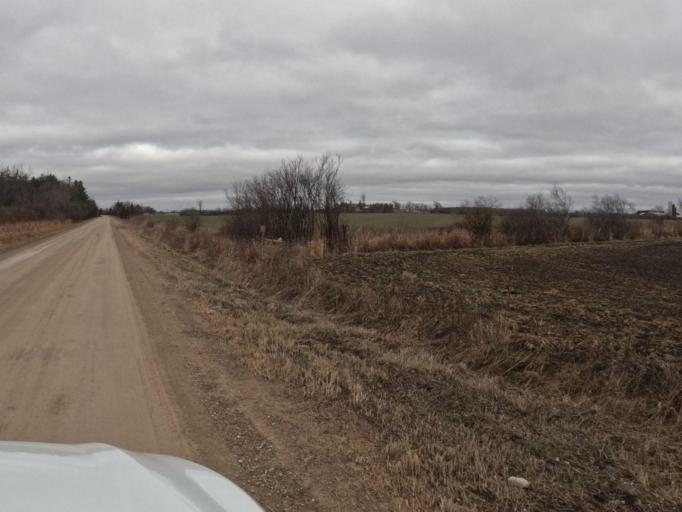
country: CA
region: Ontario
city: Shelburne
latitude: 43.9515
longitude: -80.3970
